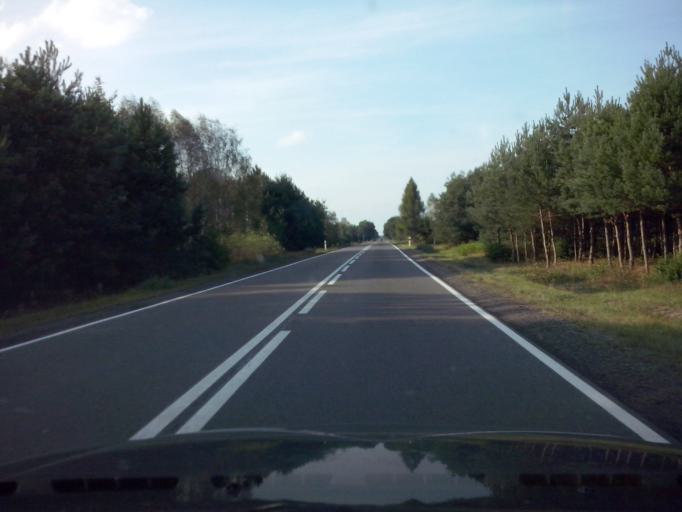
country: PL
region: Subcarpathian Voivodeship
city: Nowa Sarzyna
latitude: 50.3363
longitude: 22.3317
